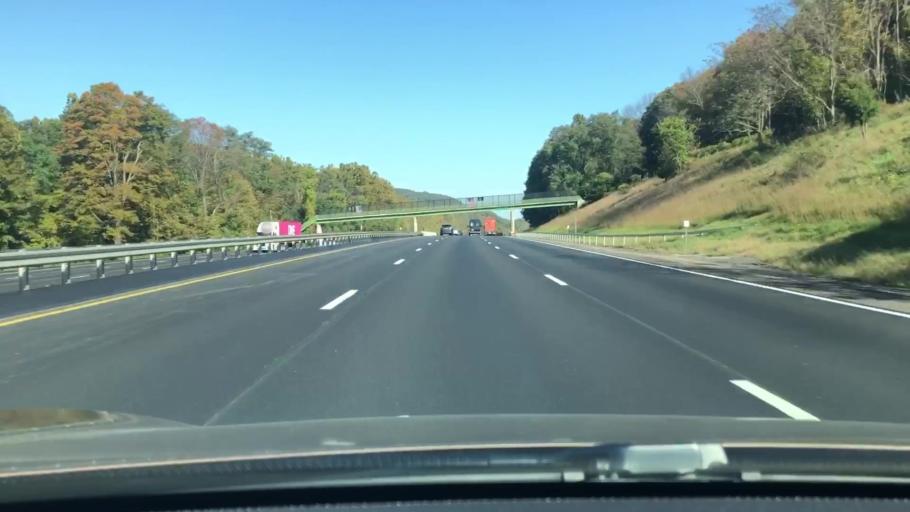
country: US
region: New York
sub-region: Orange County
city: Harriman
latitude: 41.2430
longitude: -74.1707
